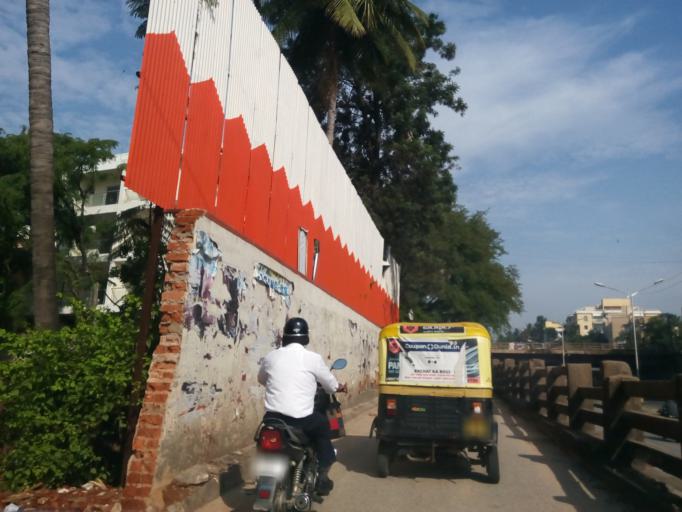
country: IN
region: Karnataka
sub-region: Bangalore Urban
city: Bangalore
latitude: 12.9937
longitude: 77.6067
